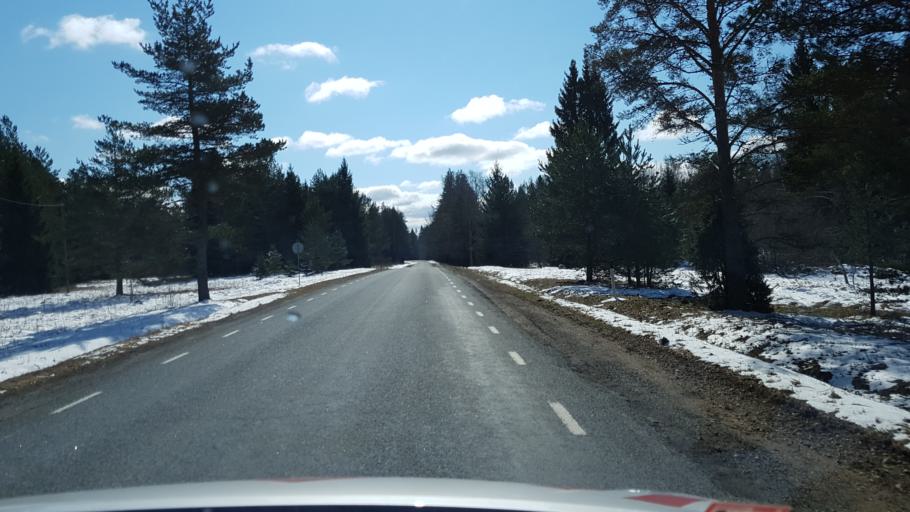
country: EE
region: Laeaene-Virumaa
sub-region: Tapa vald
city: Tapa
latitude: 59.5025
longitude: 25.9665
